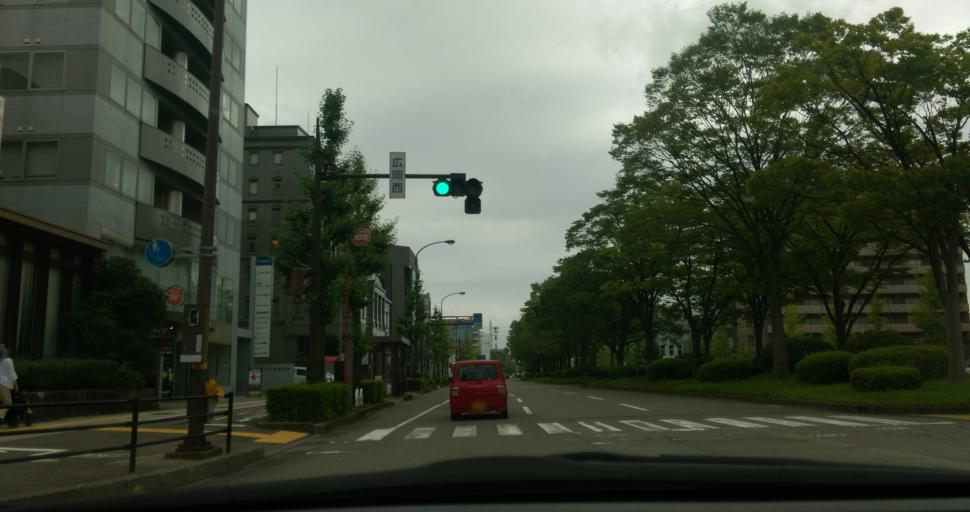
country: JP
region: Ishikawa
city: Kanazawa-shi
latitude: 36.5806
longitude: 136.6431
